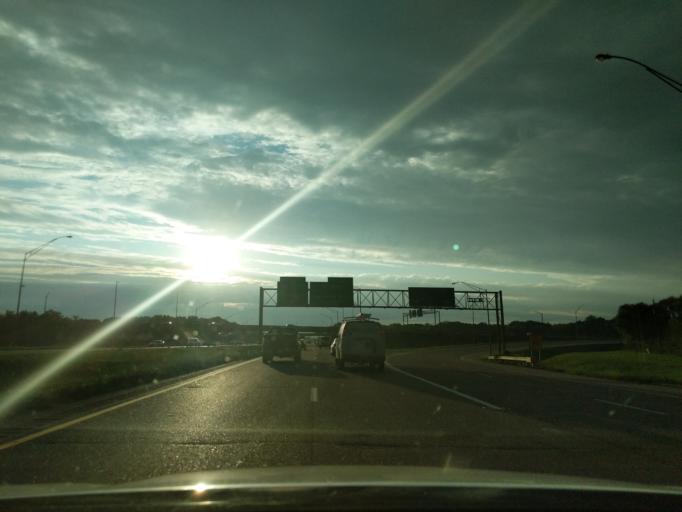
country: US
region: Tennessee
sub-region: Shelby County
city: New South Memphis
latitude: 35.0719
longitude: -90.0233
